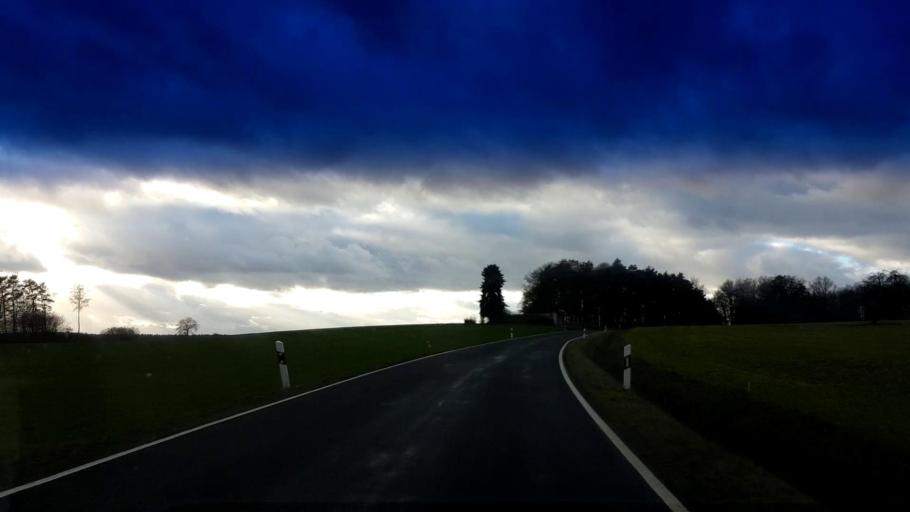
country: DE
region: Bavaria
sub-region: Upper Franconia
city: Lauter
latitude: 50.0021
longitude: 10.7637
